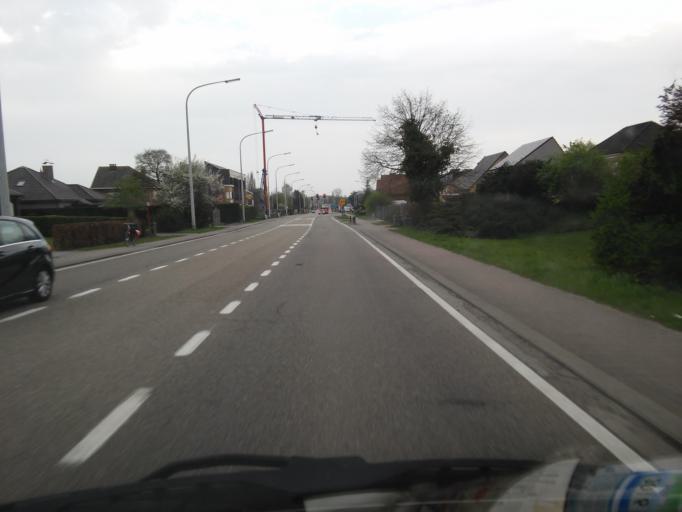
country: BE
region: Flanders
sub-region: Provincie Antwerpen
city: Rumst
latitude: 51.0877
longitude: 4.4519
